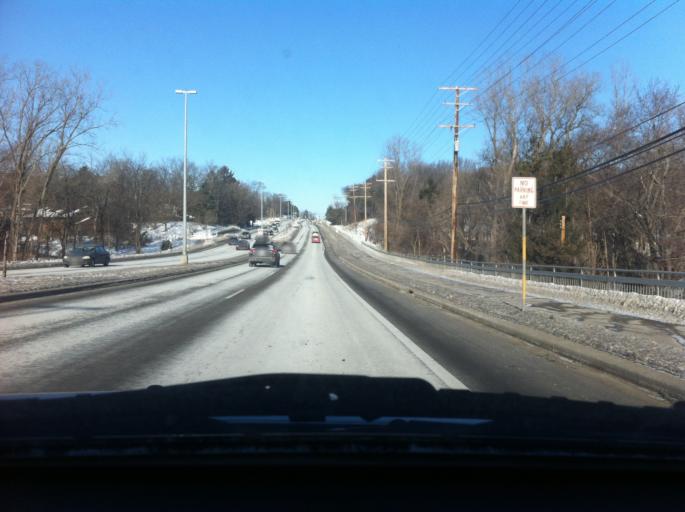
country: US
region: Wisconsin
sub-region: Dane County
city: Middleton
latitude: 43.0861
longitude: -89.4799
